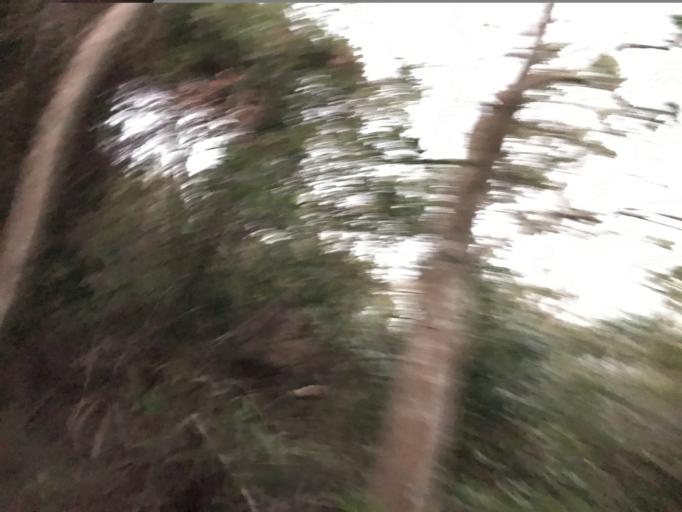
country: HK
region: Tai Po
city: Tai Po
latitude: 22.4728
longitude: 114.1450
